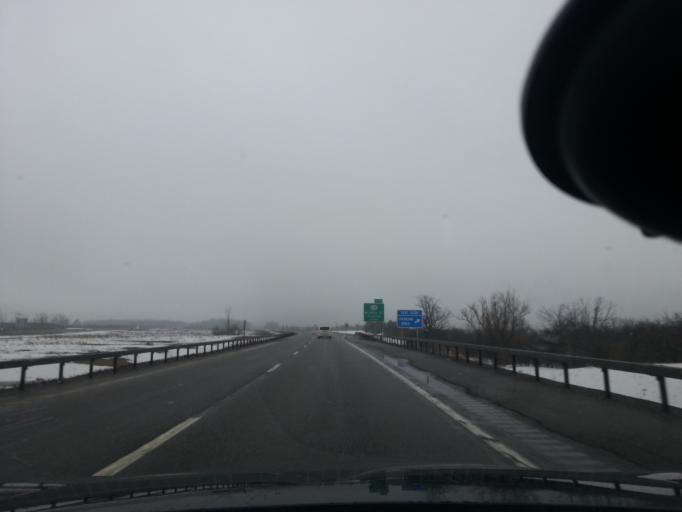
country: US
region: New York
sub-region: Jefferson County
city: Watertown
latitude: 44.0212
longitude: -75.9169
